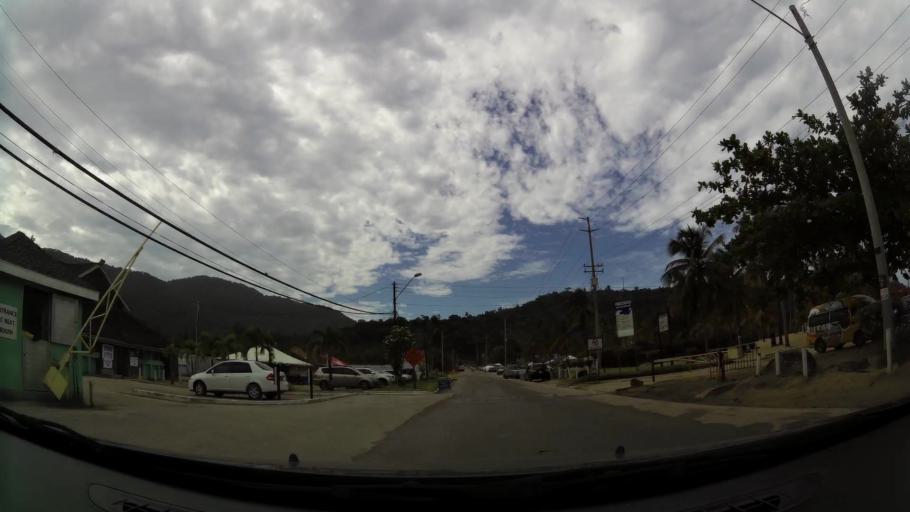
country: TT
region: Diego Martin
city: Petit Valley
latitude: 10.7581
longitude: -61.4391
